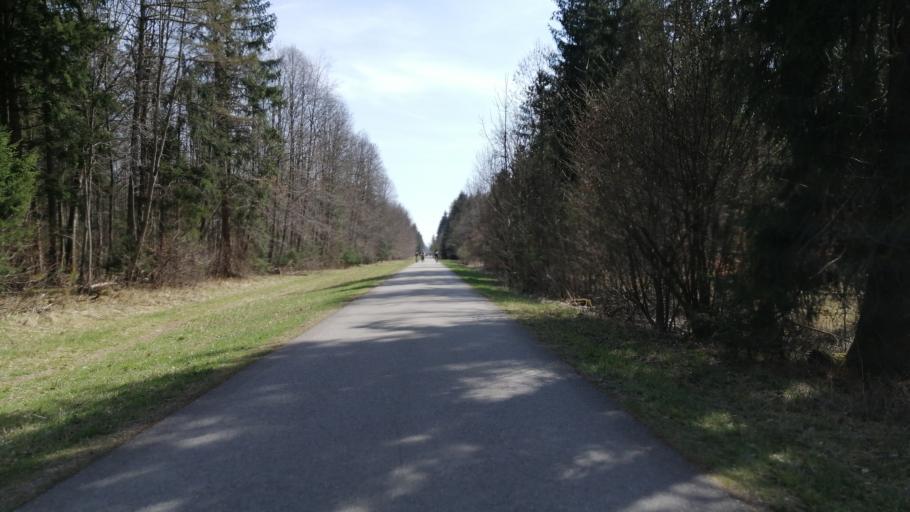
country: DE
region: Bavaria
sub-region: Upper Bavaria
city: Unterhaching
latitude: 48.0645
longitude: 11.5725
